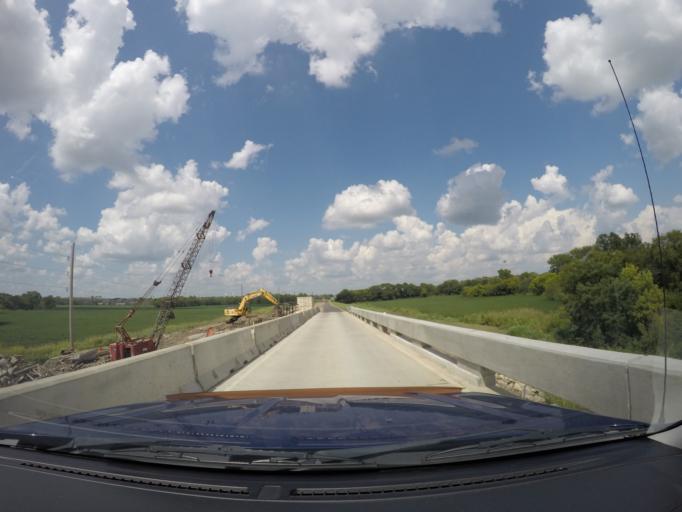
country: US
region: Kansas
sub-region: Wabaunsee County
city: Alma
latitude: 39.0015
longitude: -96.2835
